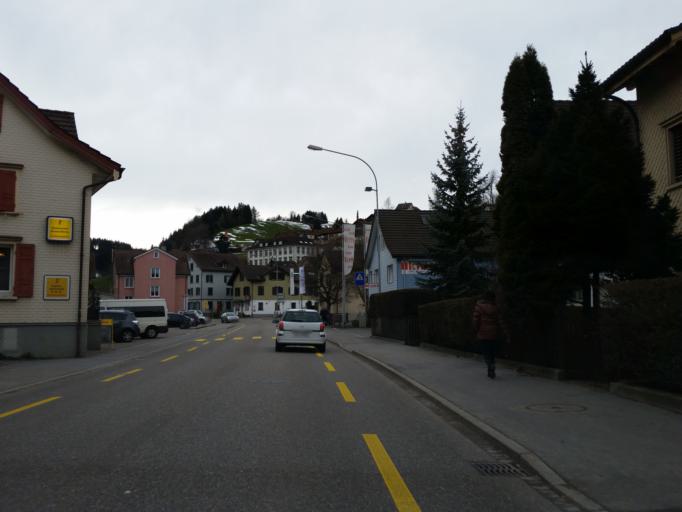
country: CH
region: Appenzell Ausserrhoden
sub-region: Bezirk Hinterland
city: Herisau
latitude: 47.3783
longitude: 9.2791
